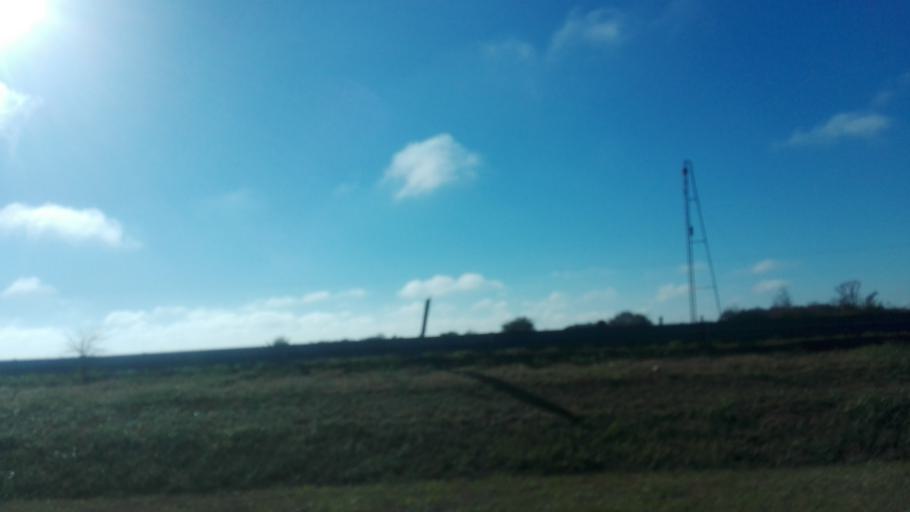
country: AR
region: Buenos Aires
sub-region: Partido de Chascomus
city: Chascomus
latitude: -35.7568
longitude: -57.9367
